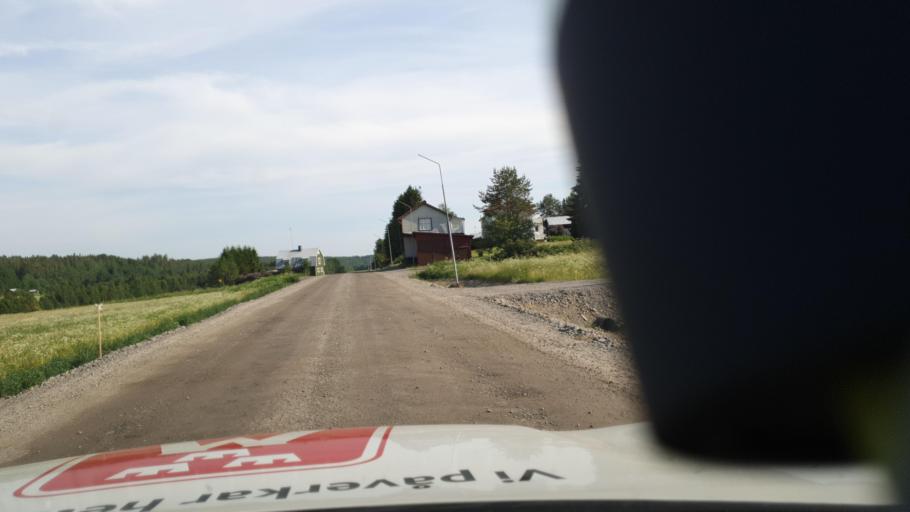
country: SE
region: Vaesterbotten
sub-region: Robertsfors Kommun
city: Robertsfors
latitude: 64.3227
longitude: 21.0205
